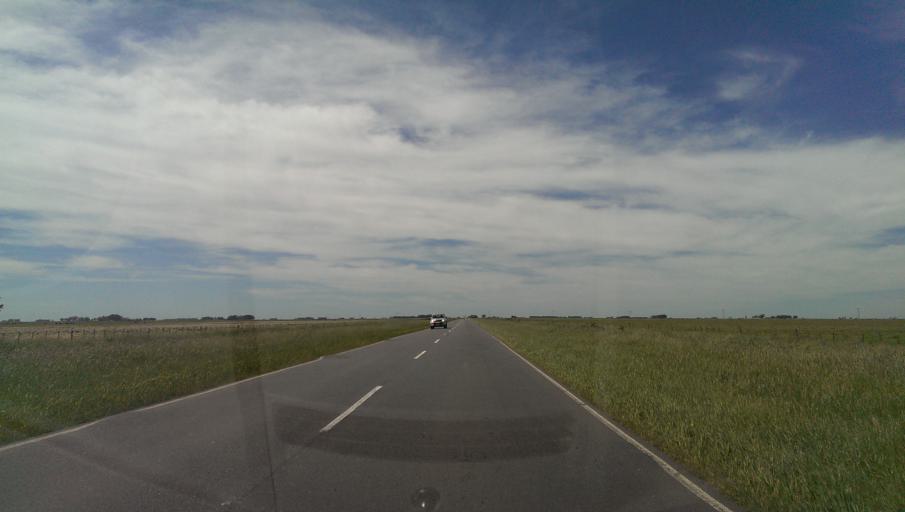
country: AR
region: Buenos Aires
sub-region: Partido de Laprida
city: Laprida
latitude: -37.2403
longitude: -60.7636
